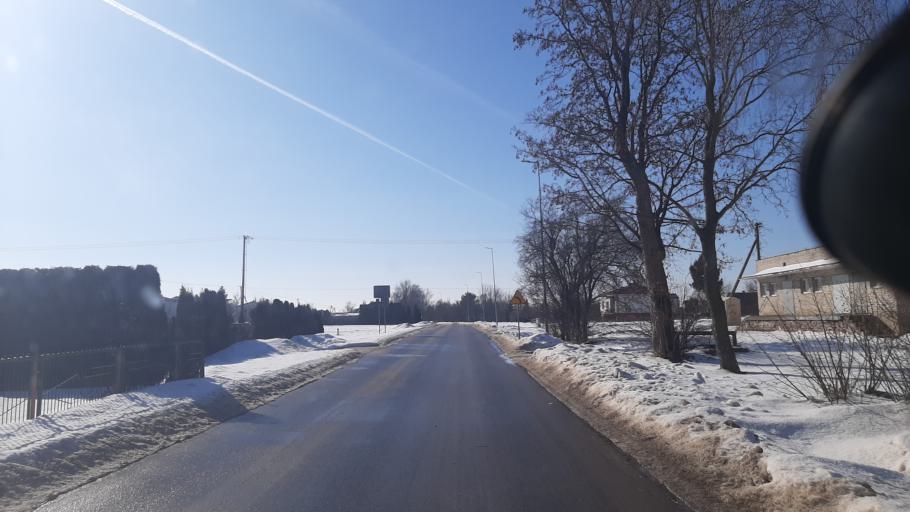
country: PL
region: Lublin Voivodeship
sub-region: Powiat lubelski
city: Garbow
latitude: 51.3042
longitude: 22.3079
